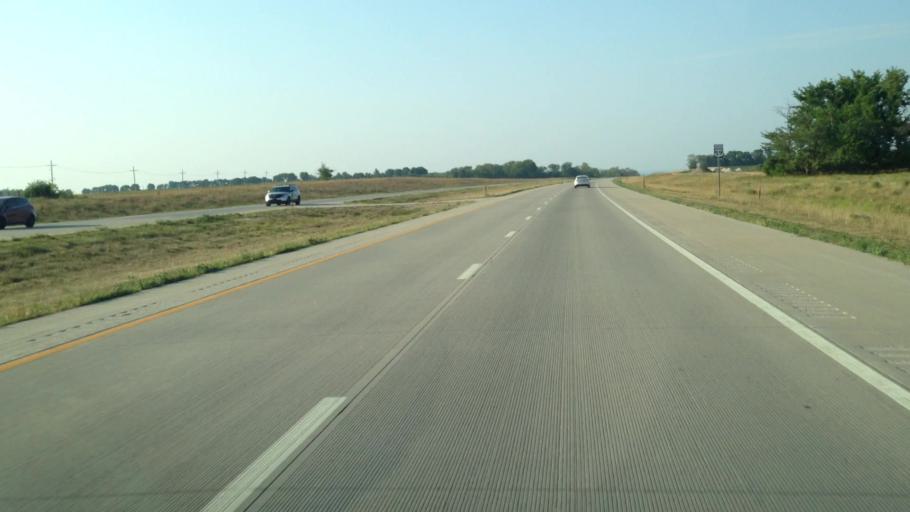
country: US
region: Kansas
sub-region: Douglas County
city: Baldwin City
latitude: 38.8396
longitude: -95.2682
